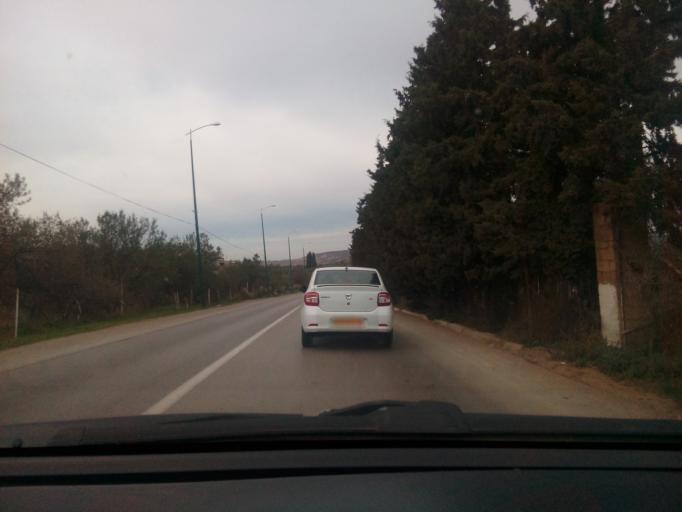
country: DZ
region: Tlemcen
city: Mansoura
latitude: 34.8638
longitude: -1.3425
